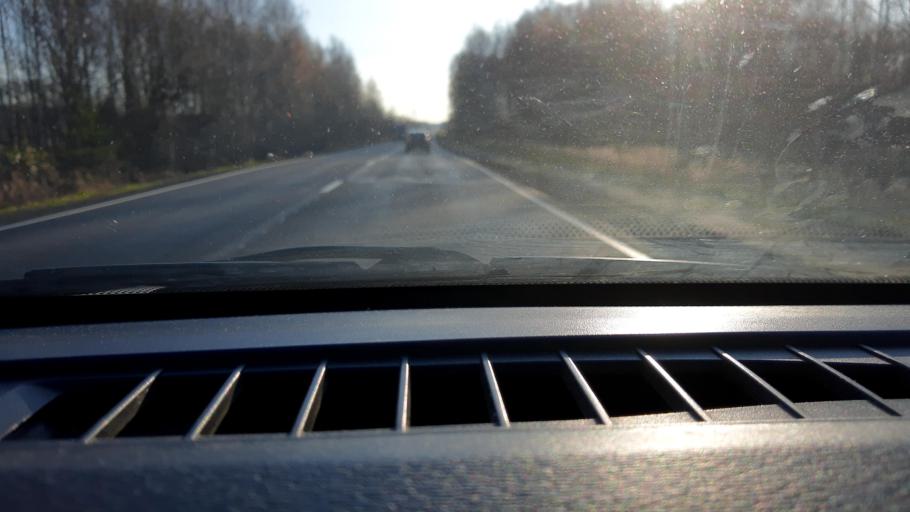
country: RU
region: Nizjnij Novgorod
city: Novaya Balakhna
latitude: 56.5903
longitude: 43.6624
